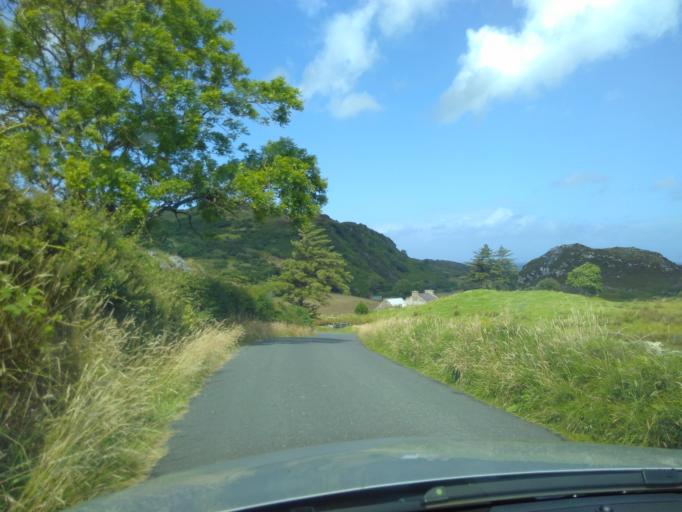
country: IE
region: Ulster
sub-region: County Donegal
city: Ramelton
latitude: 55.2228
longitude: -7.6235
